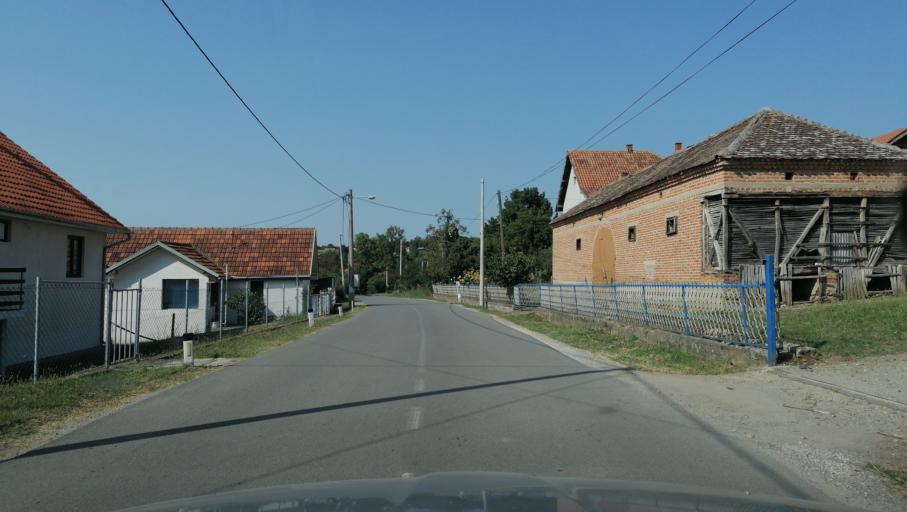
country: RS
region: Central Serbia
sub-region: Belgrade
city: Sopot
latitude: 44.5874
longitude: 20.6107
